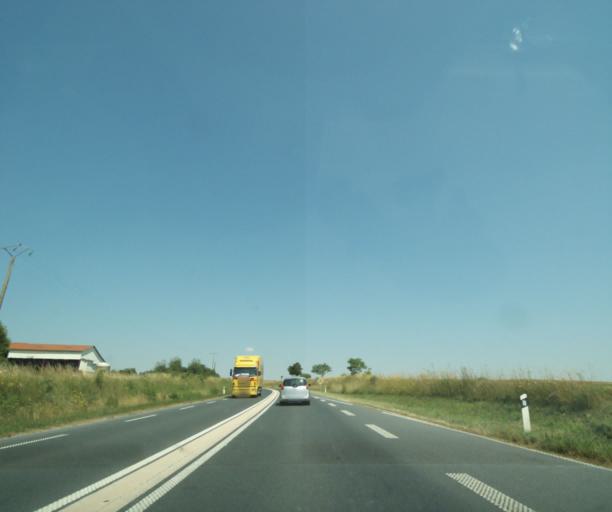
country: FR
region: Champagne-Ardenne
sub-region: Departement de la Marne
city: Mourmelon-le-Grand
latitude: 49.0670
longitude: 4.2964
